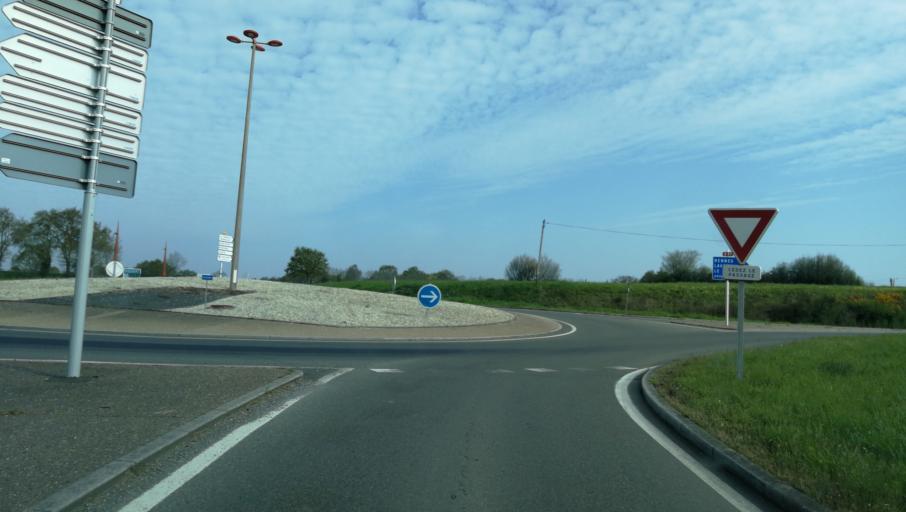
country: FR
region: Pays de la Loire
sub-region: Departement de la Mayenne
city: Vaiges
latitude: 48.0553
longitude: -0.4897
